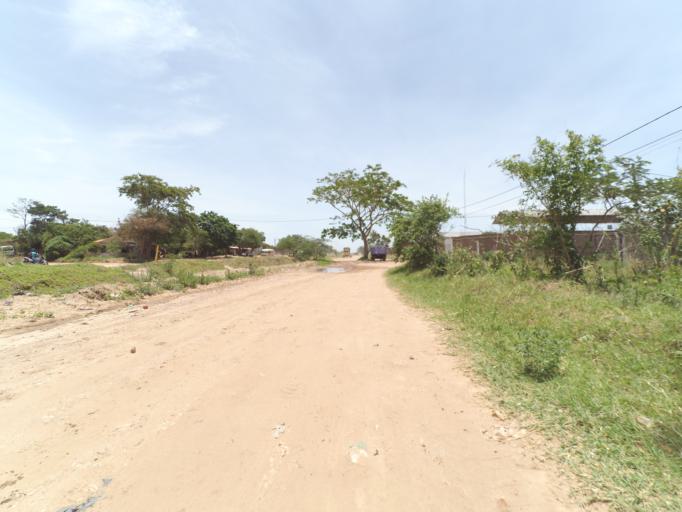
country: BO
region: Santa Cruz
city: Santa Cruz de la Sierra
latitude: -17.8256
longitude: -63.2452
